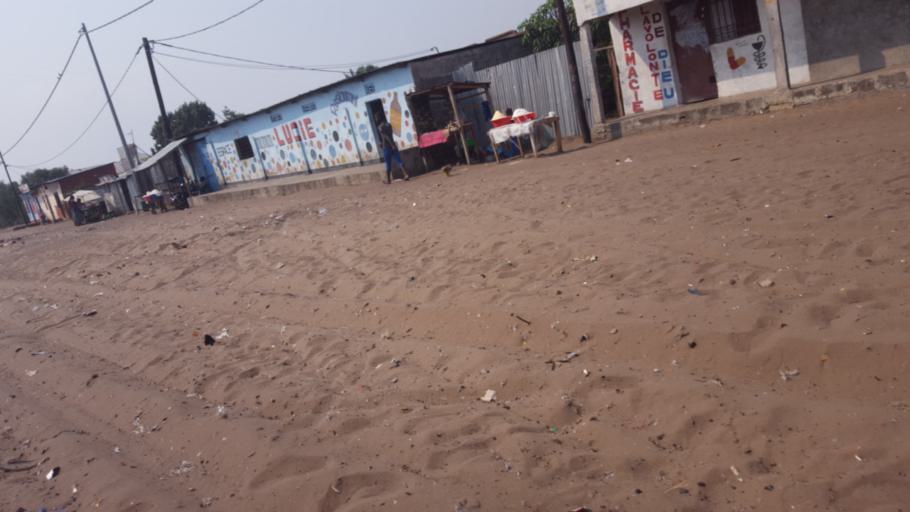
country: CD
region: Kinshasa
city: Masina
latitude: -4.3674
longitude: 15.5137
